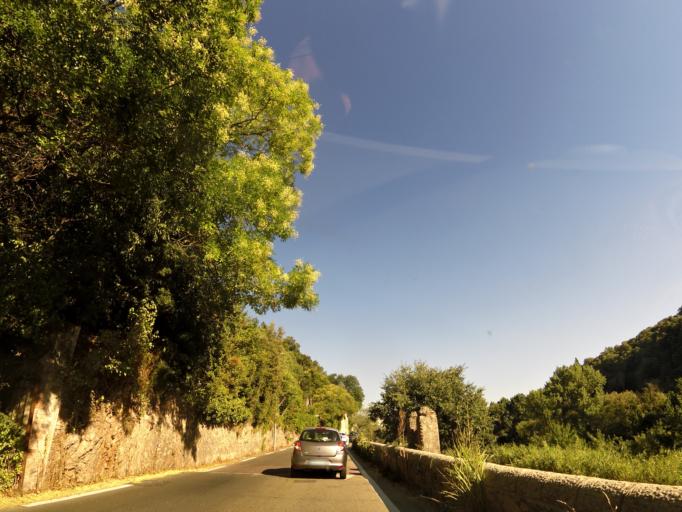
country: FR
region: Languedoc-Roussillon
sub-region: Departement de l'Herault
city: Ganges
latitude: 43.9363
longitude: 3.6969
